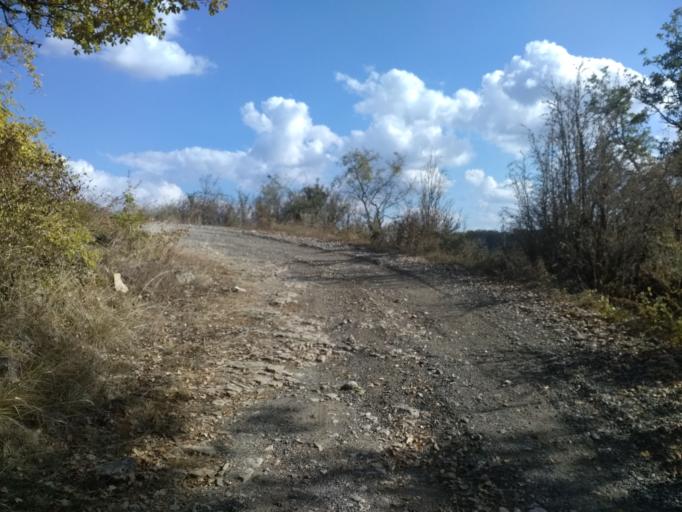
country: FR
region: Midi-Pyrenees
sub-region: Departement de l'Aveyron
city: Bozouls
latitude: 44.4765
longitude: 2.6891
